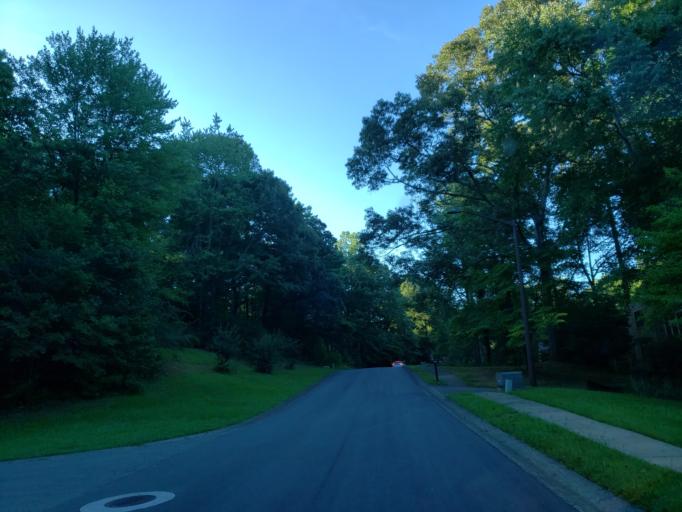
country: US
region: Georgia
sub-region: Fulton County
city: Roswell
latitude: 34.0116
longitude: -84.4501
